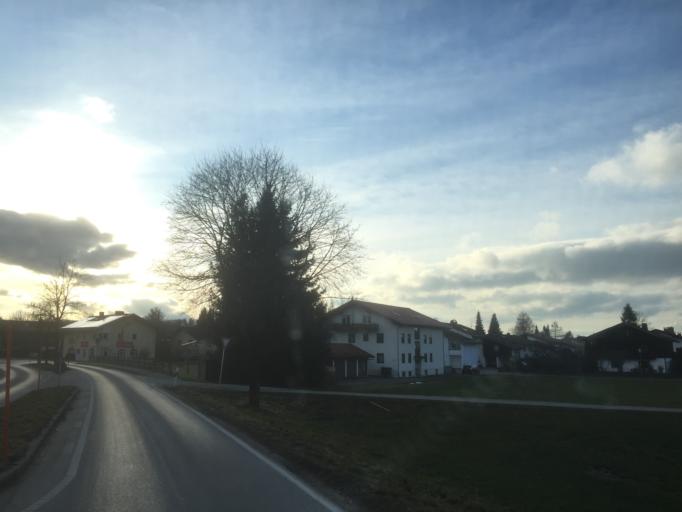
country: DE
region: Bavaria
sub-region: Upper Bavaria
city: Vachendorf
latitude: 47.8441
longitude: 12.6088
